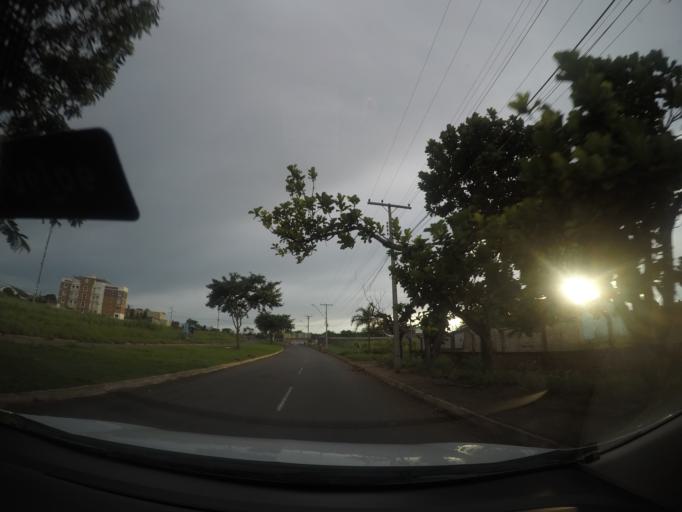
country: BR
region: Goias
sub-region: Goiania
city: Goiania
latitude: -16.7466
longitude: -49.3185
